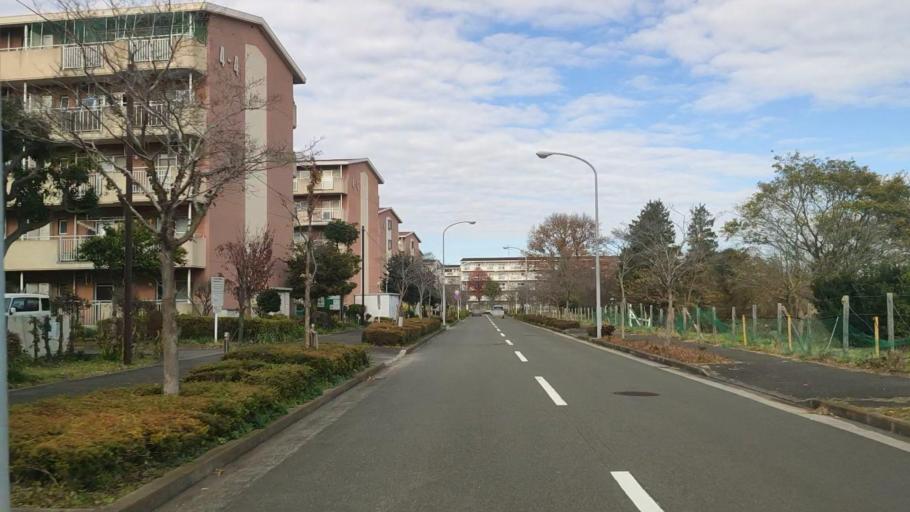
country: JP
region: Kanagawa
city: Minami-rinkan
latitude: 35.4811
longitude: 139.4906
